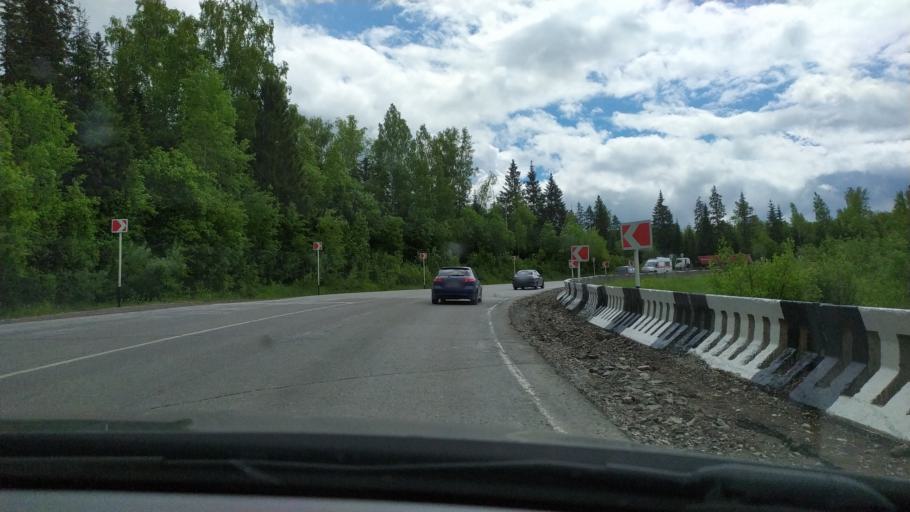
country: RU
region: Perm
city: Gremyachinsk
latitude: 58.4412
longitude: 57.8872
